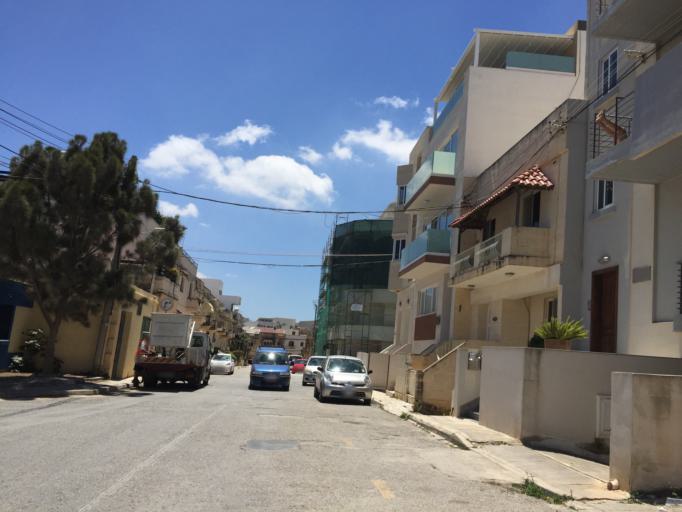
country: MT
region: Is-Swieqi
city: Swieqi
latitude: 35.9217
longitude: 14.4823
